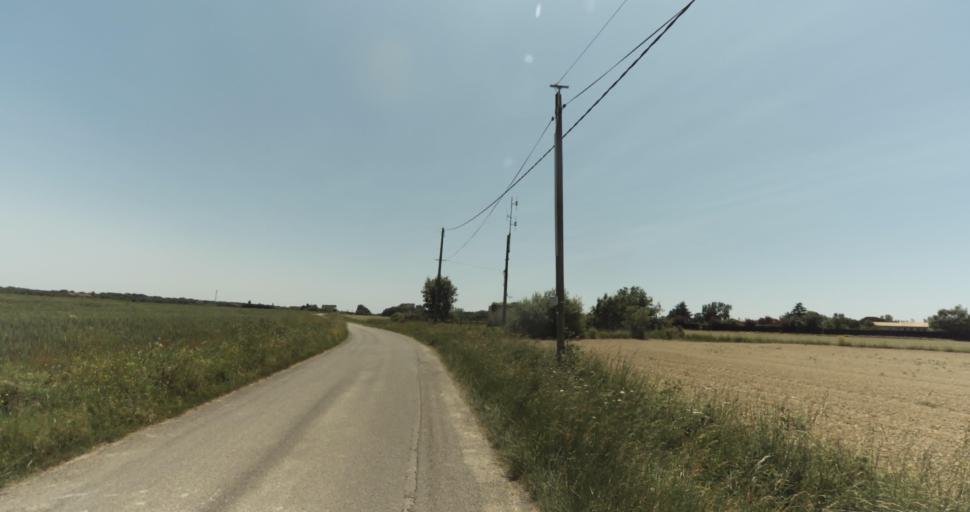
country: FR
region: Midi-Pyrenees
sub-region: Departement de la Haute-Garonne
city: Levignac
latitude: 43.6472
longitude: 1.1903
